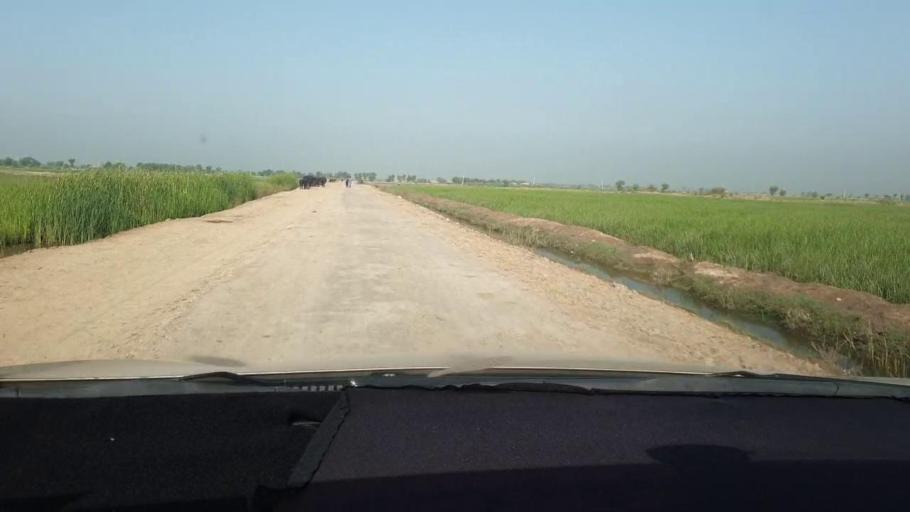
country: PK
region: Sindh
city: Miro Khan
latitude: 27.7567
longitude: 68.1394
